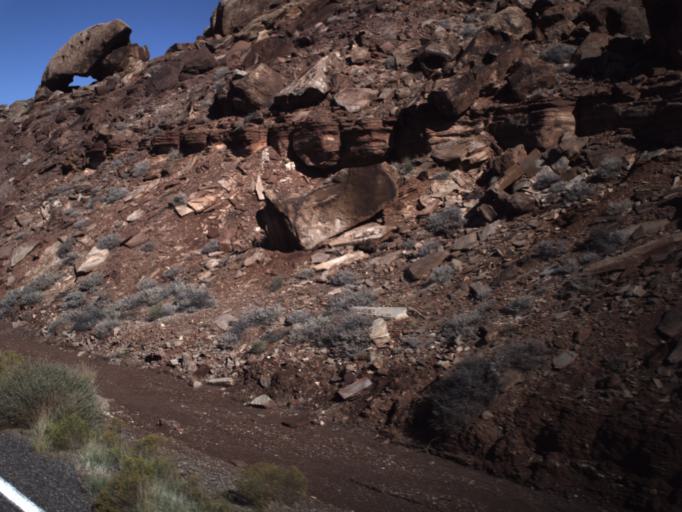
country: US
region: Utah
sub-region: San Juan County
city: Blanding
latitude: 37.8824
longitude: -110.4232
